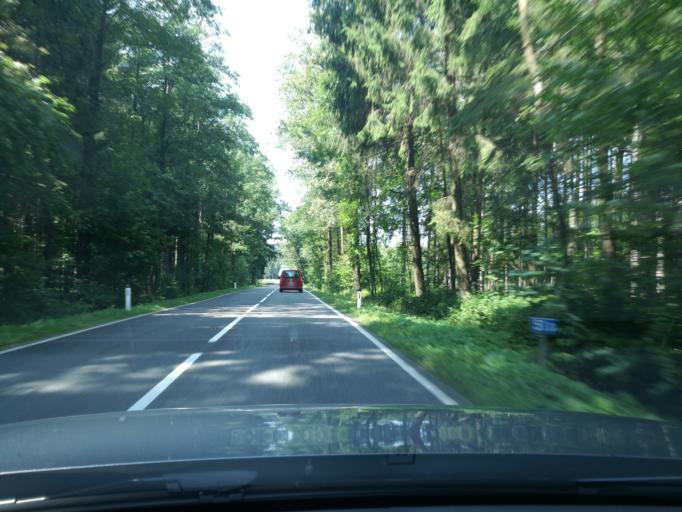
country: AT
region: Upper Austria
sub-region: Politischer Bezirk Grieskirchen
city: Grieskirchen
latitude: 48.3512
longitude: 13.7210
